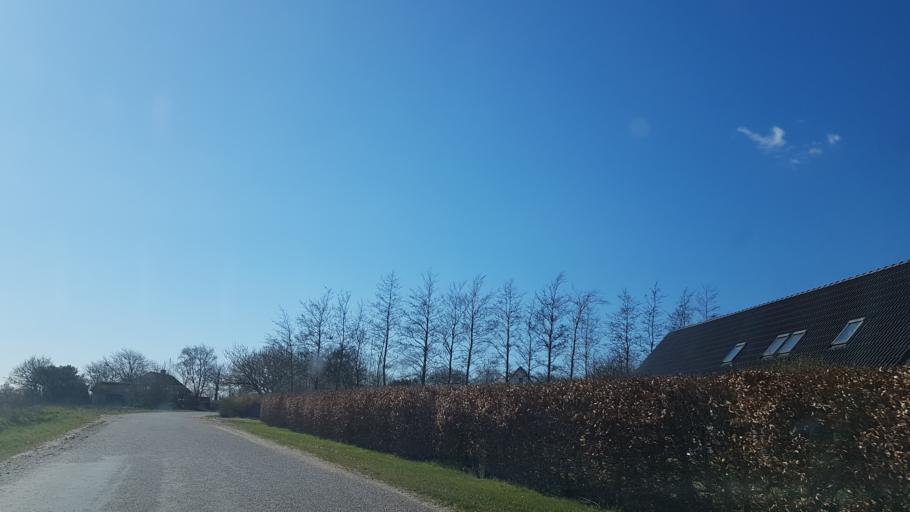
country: DK
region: South Denmark
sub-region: Esbjerg Kommune
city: Ribe
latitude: 55.2525
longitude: 8.7008
